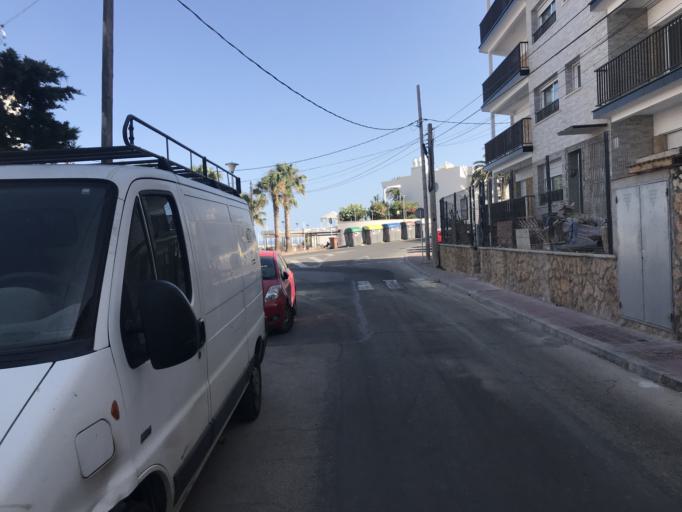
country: ES
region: Catalonia
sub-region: Provincia de Tarragona
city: Torredembarra
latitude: 41.1380
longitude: 1.4009
